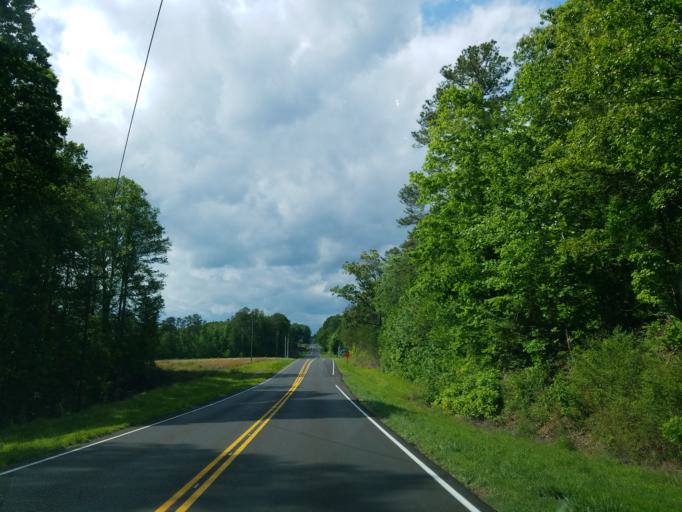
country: US
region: Georgia
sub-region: Pickens County
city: Jasper
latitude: 34.4394
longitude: -84.3983
